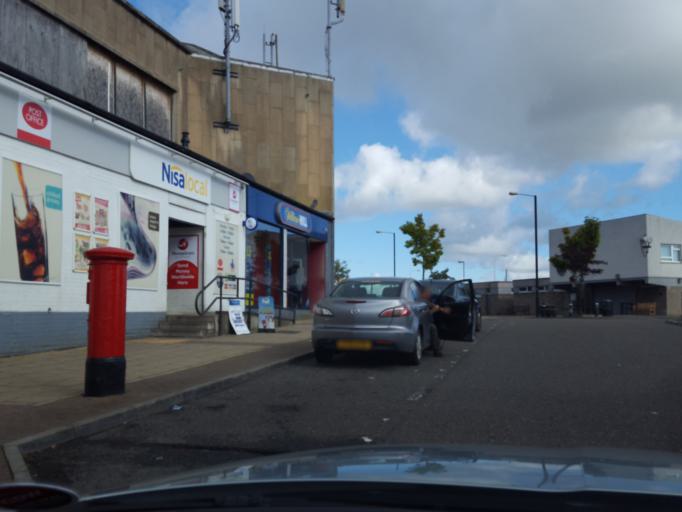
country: GB
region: Scotland
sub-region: Fife
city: Townhill
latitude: 56.0658
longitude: -3.4252
